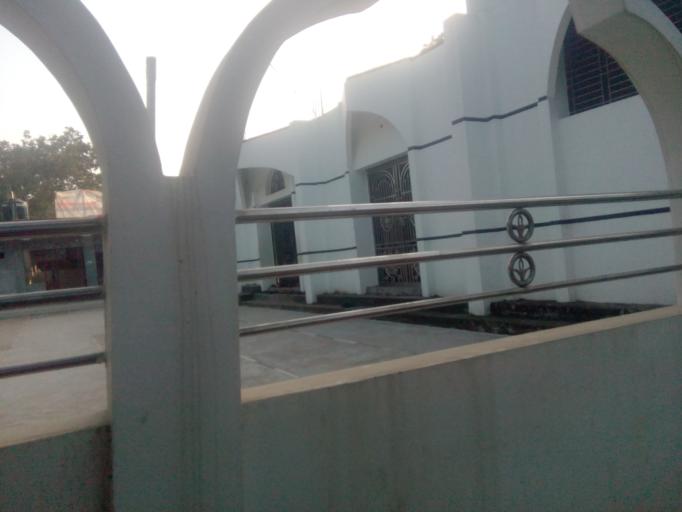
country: BD
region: Chittagong
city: Comilla
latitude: 23.4121
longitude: 91.2302
